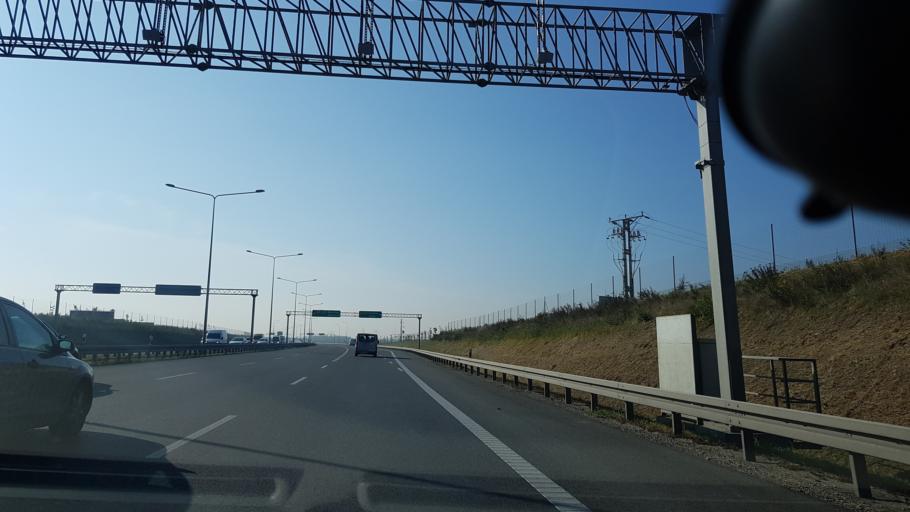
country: PL
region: Masovian Voivodeship
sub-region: Powiat pruszkowski
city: Nowe Grocholice
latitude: 52.1416
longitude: 20.8837
